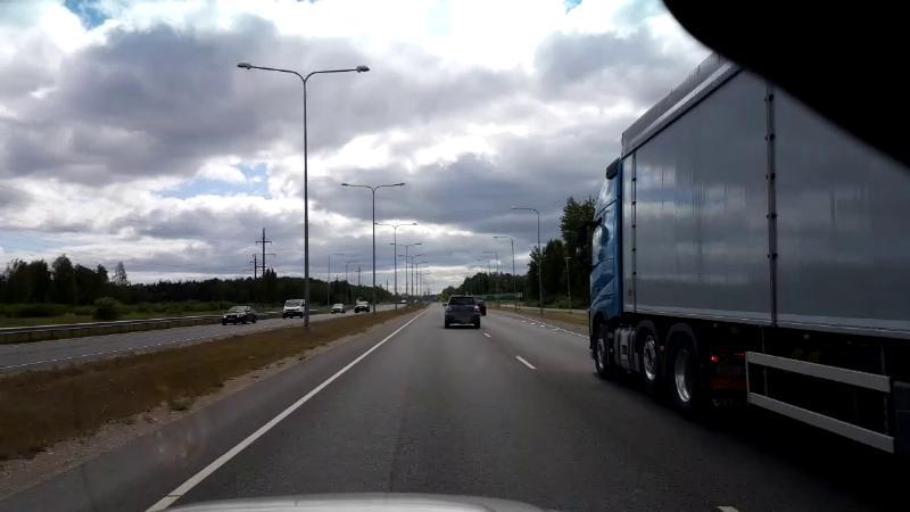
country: EE
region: Paernumaa
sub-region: Paernu linn
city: Parnu
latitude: 58.3897
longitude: 24.5474
